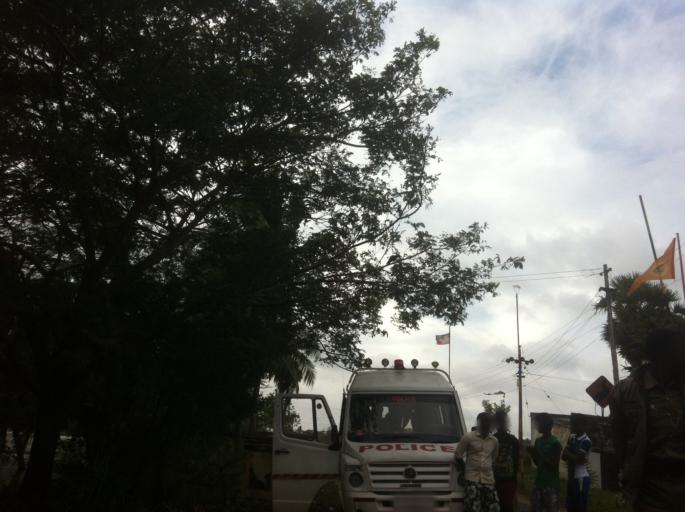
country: IN
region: Tamil Nadu
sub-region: Villupuram
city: Marakkanam
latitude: 12.1043
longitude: 79.9010
